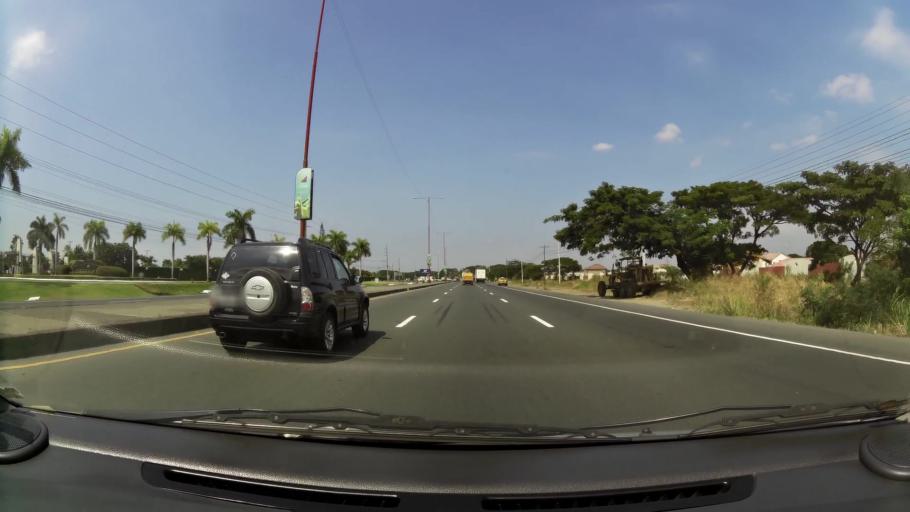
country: EC
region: Guayas
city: Eloy Alfaro
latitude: -2.0511
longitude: -79.9001
